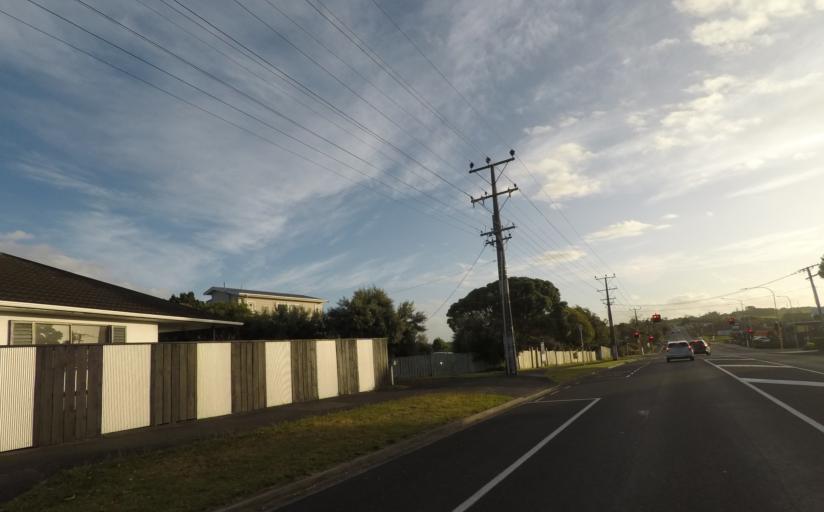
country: NZ
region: Auckland
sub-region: Auckland
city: Rosebank
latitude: -36.8055
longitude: 174.6374
